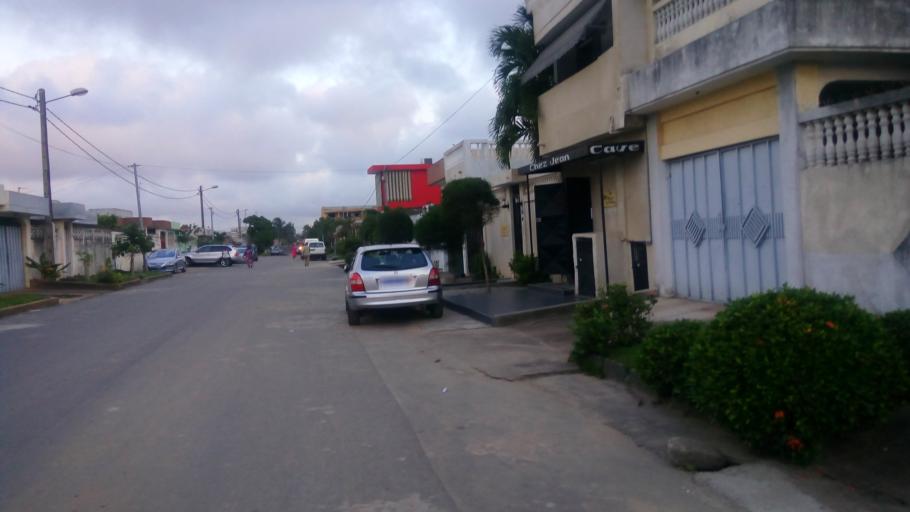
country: CI
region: Lagunes
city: Abobo
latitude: 5.4091
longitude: -3.9898
